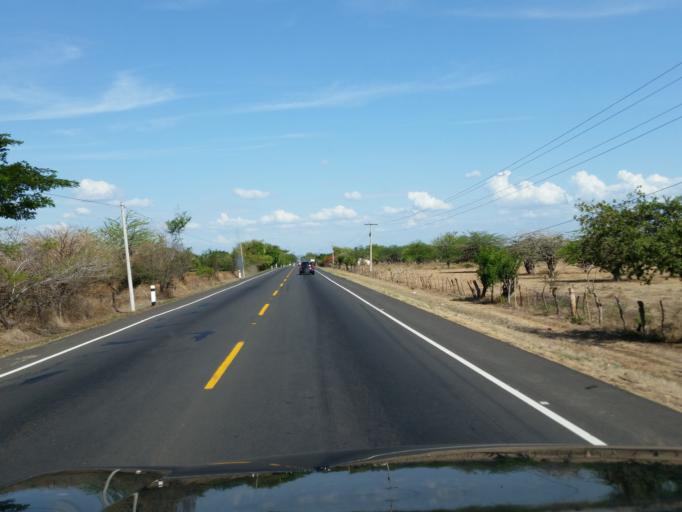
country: NI
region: Leon
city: La Paz Centro
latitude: 12.3196
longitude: -86.7935
